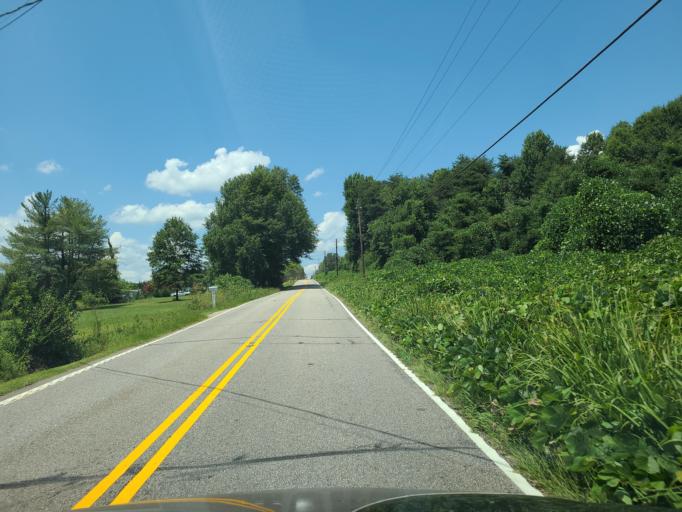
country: US
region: South Carolina
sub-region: Spartanburg County
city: Duncan
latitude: 34.9797
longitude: -82.1766
